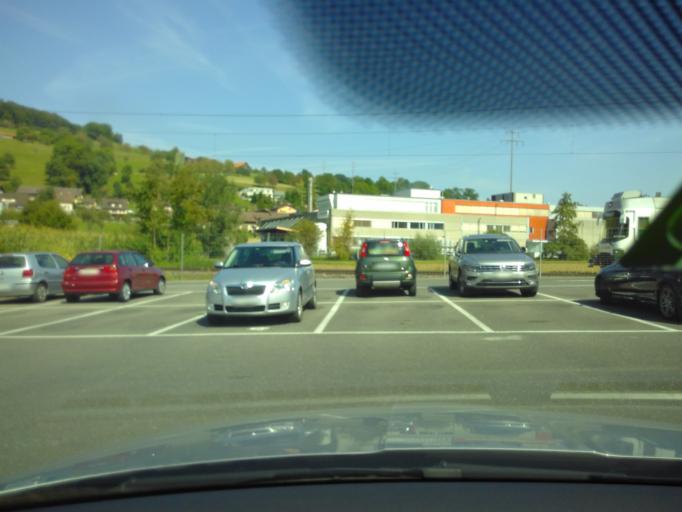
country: CH
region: Aargau
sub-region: Bezirk Kulm
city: Reinach
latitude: 47.2649
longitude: 8.1772
